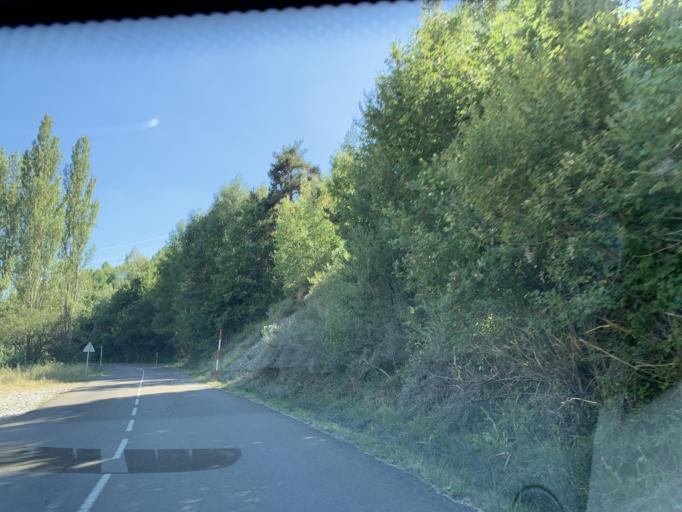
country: ES
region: Aragon
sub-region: Provincia de Huesca
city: Hoz de Jaca
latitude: 42.7036
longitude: -0.3229
